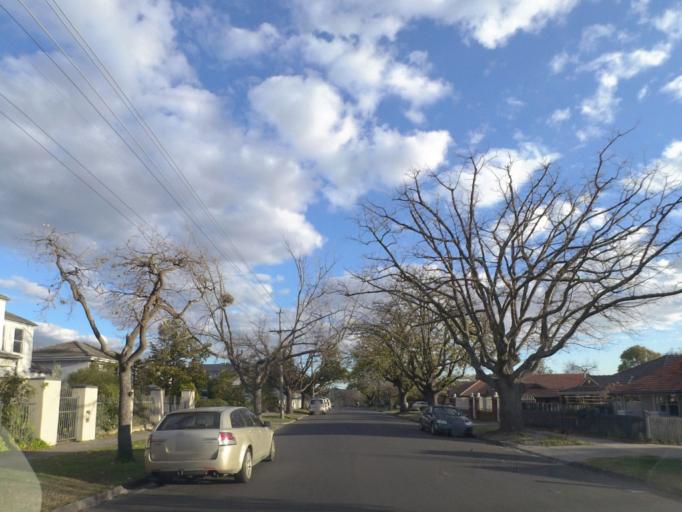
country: AU
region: Victoria
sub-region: Whitehorse
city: Surrey Hills
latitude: -37.8383
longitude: 145.0930
